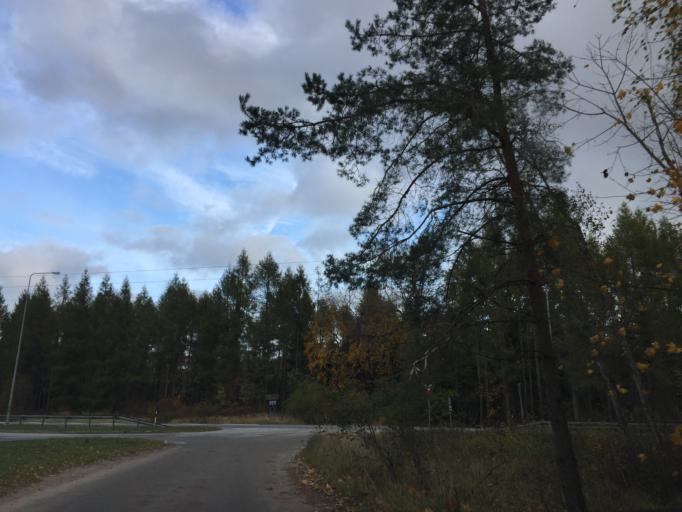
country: LV
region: Salacgrivas
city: Salacgriva
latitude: 57.5694
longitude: 24.4338
